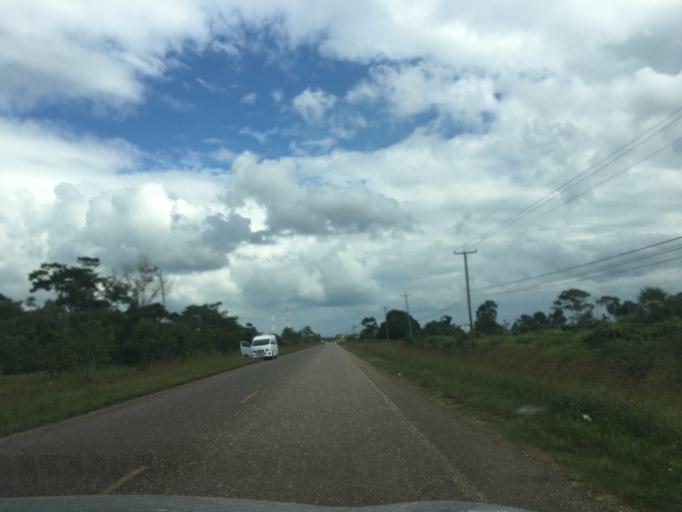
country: BZ
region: Stann Creek
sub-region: Dangriga
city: Dangriga
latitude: 16.8776
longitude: -88.3444
